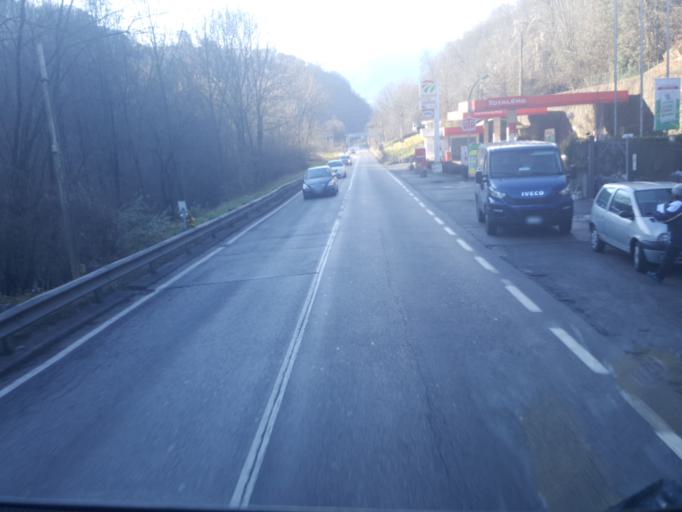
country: IT
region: Lombardy
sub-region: Provincia di Bergamo
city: Casnigo
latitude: 45.8048
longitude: 9.8670
